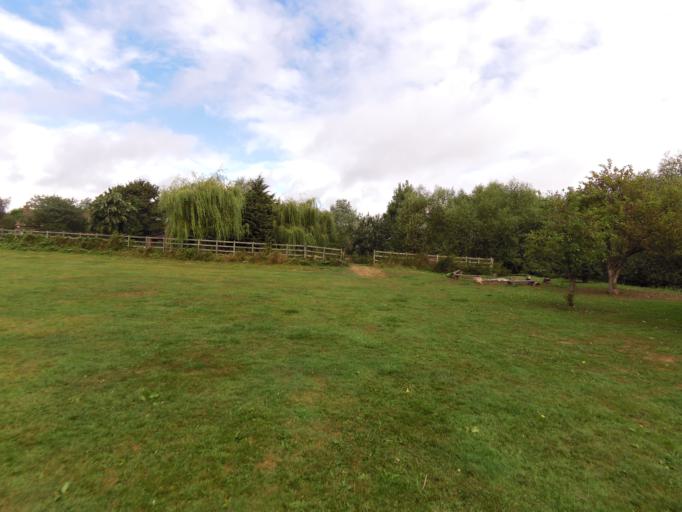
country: GB
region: England
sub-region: Hertfordshire
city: Radlett
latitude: 51.7084
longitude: -0.3156
